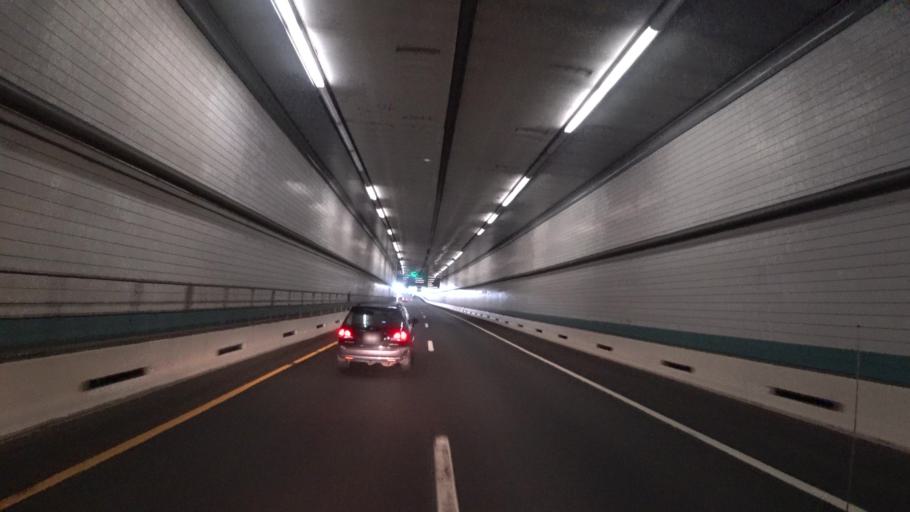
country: US
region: Massachusetts
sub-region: Suffolk County
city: Chelsea
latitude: 42.3631
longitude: -71.0265
